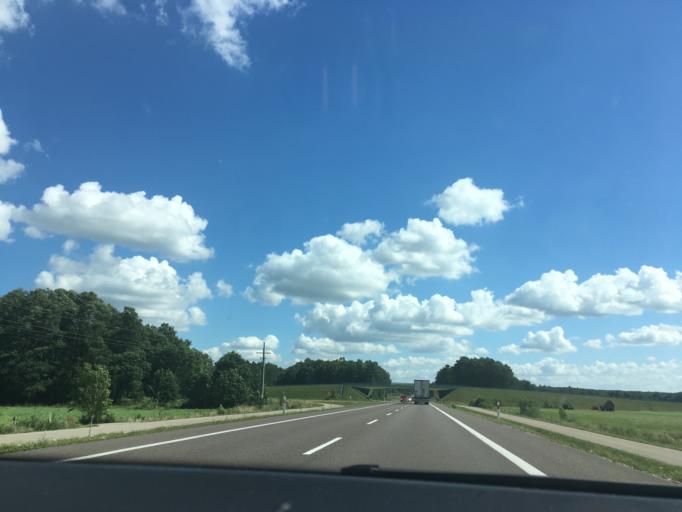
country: PL
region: Podlasie
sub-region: Powiat augustowski
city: Augustow
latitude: 53.7530
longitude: 23.0890
